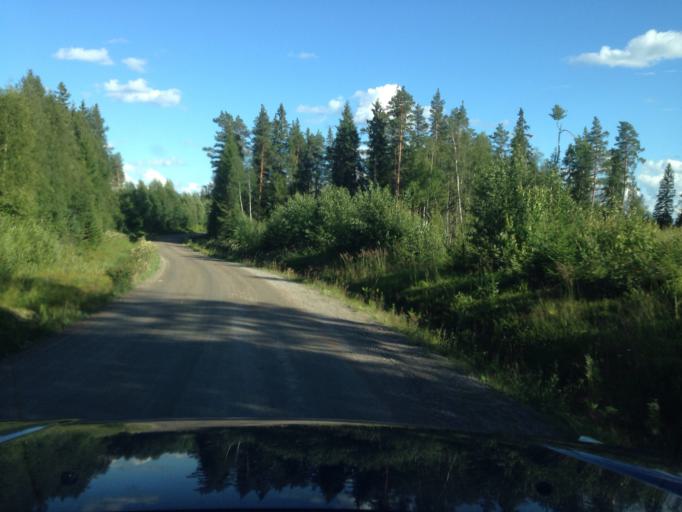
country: SE
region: Dalarna
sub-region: Ludvika Kommun
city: Abborrberget
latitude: 60.2301
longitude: 14.8378
